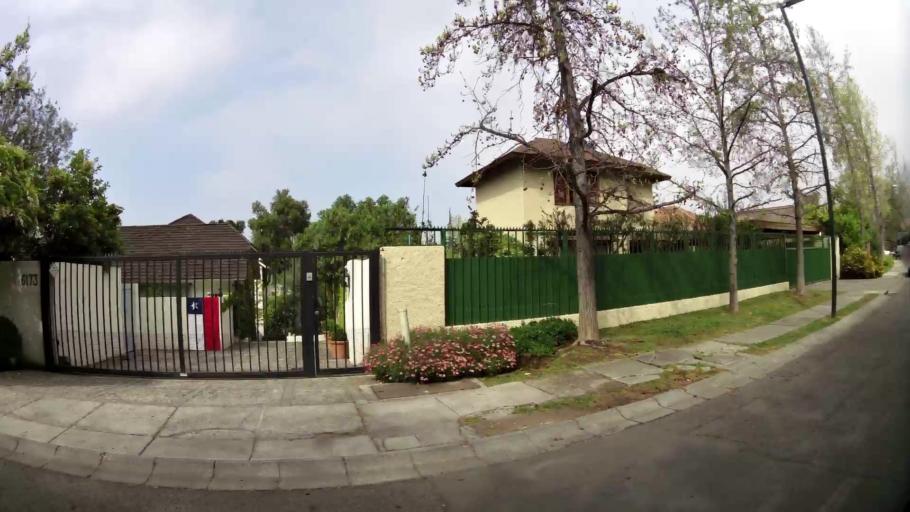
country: CL
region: Santiago Metropolitan
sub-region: Provincia de Santiago
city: Villa Presidente Frei, Nunoa, Santiago, Chile
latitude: -33.3701
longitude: -70.5821
